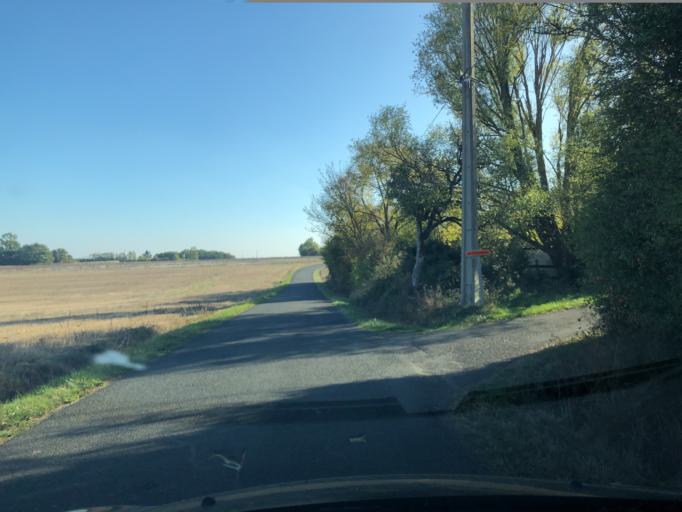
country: FR
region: Centre
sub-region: Departement d'Indre-et-Loire
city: Neuvy-le-Roi
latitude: 47.6643
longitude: 0.6086
